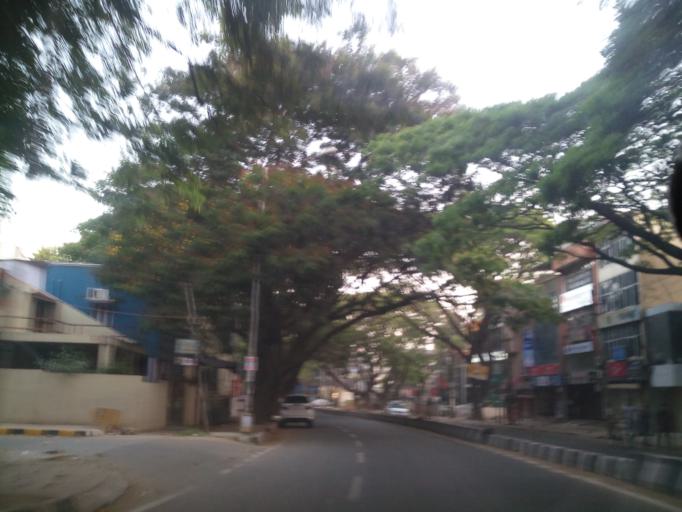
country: IN
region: Karnataka
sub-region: Bangalore Urban
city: Bangalore
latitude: 12.9301
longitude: 77.6331
